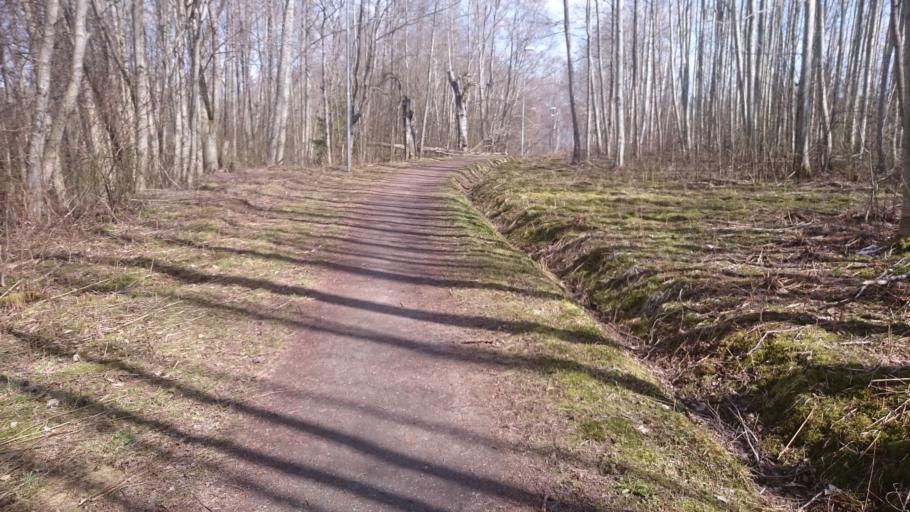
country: SE
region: OErebro
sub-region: Karlskoga Kommun
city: Karlskoga
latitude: 59.3047
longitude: 14.5161
